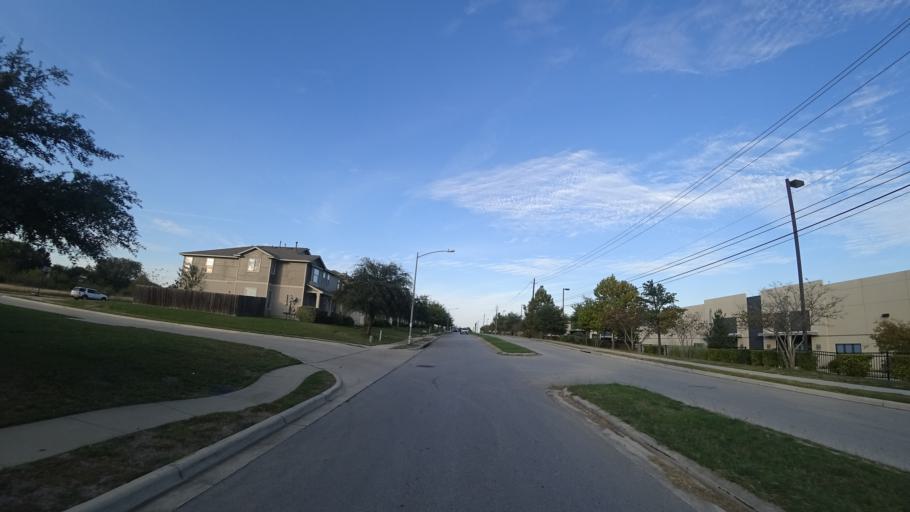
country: US
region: Texas
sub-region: Travis County
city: Pflugerville
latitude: 30.4117
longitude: -97.6472
